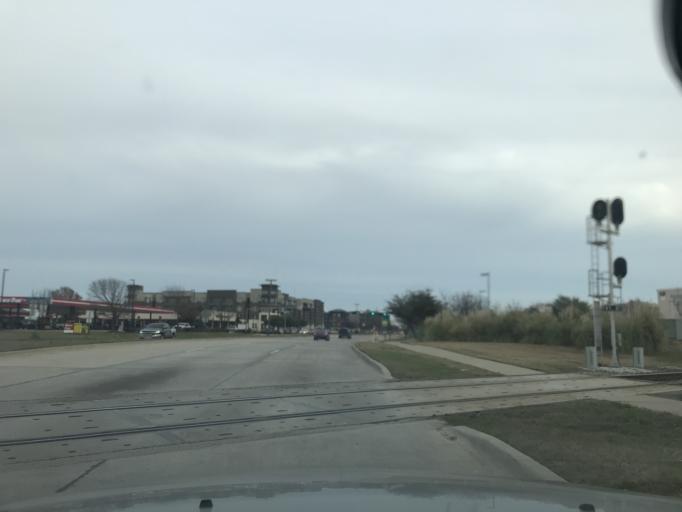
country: US
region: Texas
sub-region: Dallas County
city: Carrollton
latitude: 32.9938
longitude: -96.9395
